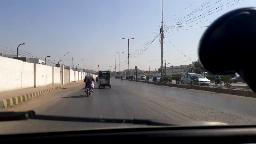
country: PK
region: Sindh
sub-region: Karachi District
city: Karachi
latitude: 24.8952
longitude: 67.0912
